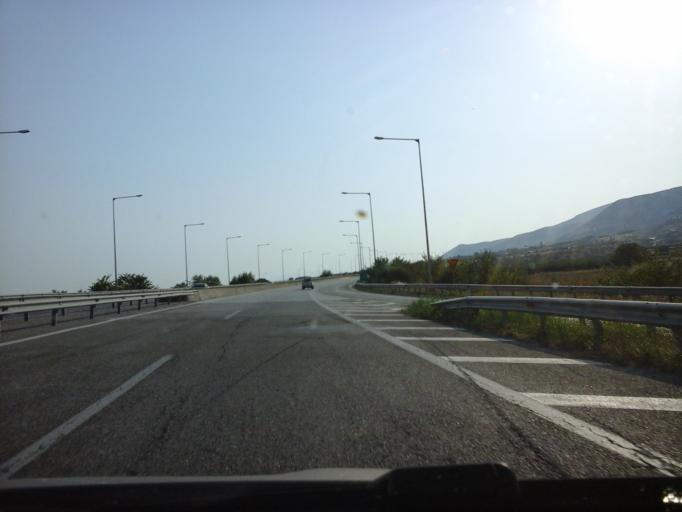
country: GR
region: East Macedonia and Thrace
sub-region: Nomos Kavalas
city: Chrysoupolis
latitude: 40.9905
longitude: 24.6363
